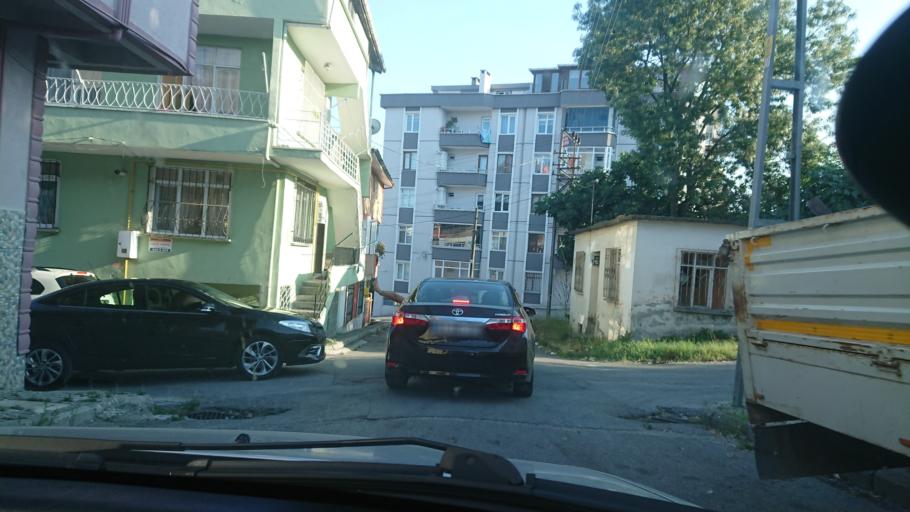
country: TR
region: Samsun
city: Samsun
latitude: 41.2975
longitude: 36.3212
